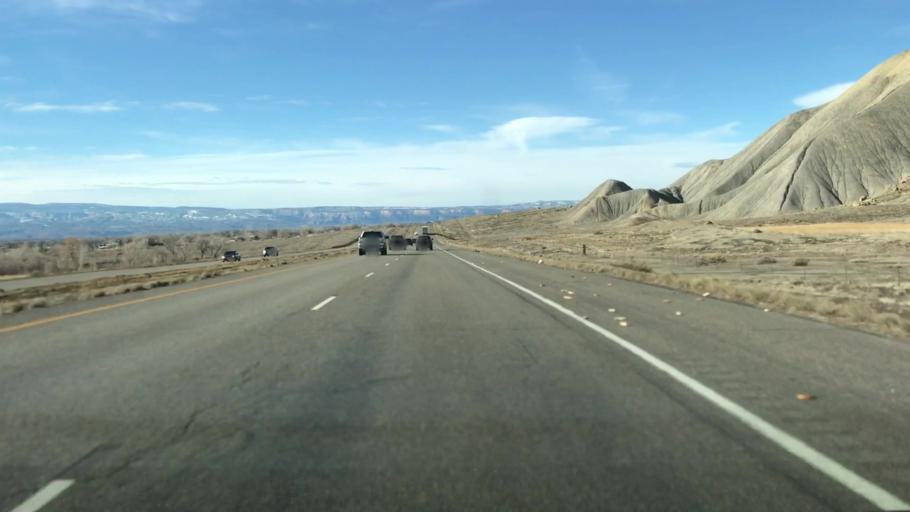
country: US
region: Colorado
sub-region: Mesa County
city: Palisade
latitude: 39.1150
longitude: -108.4009
